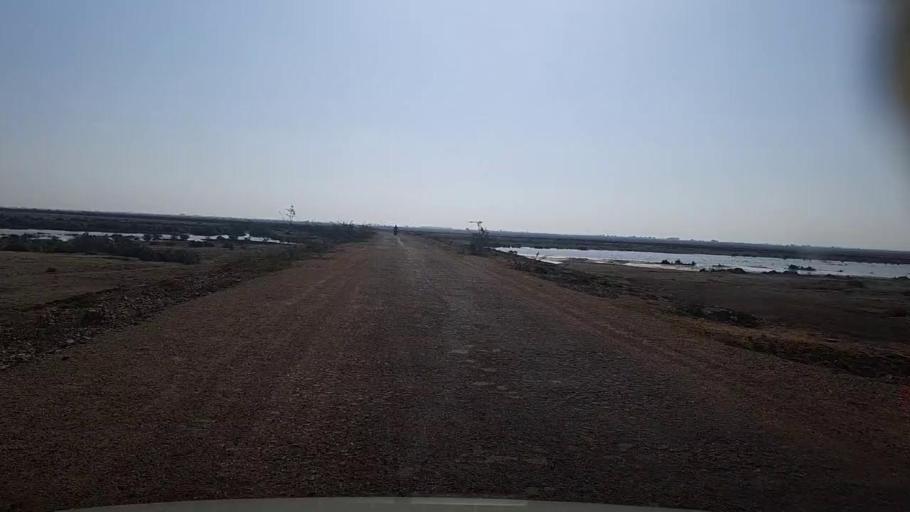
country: PK
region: Sindh
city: Mirpur Sakro
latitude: 24.5183
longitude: 67.4920
